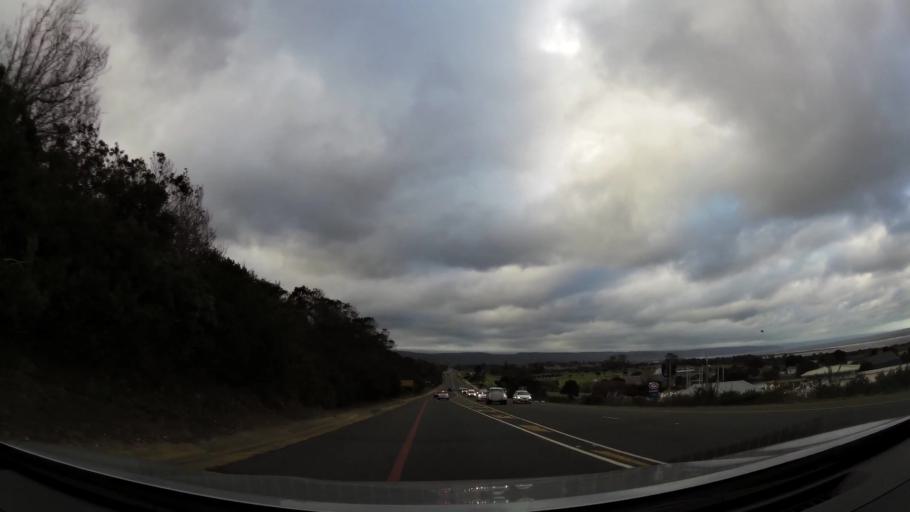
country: ZA
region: Western Cape
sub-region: Eden District Municipality
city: Plettenberg Bay
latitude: -34.0416
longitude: 23.3689
